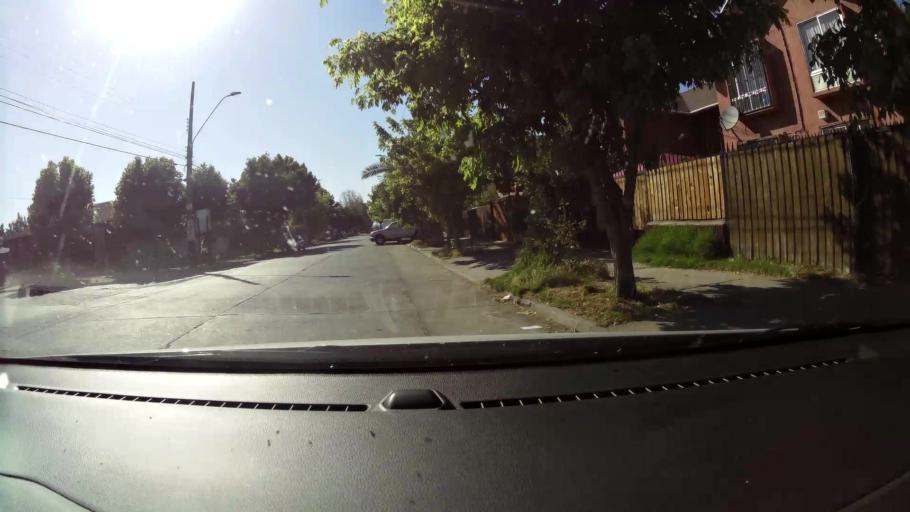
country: CL
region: Santiago Metropolitan
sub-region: Provincia de Maipo
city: San Bernardo
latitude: -33.6021
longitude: -70.6948
